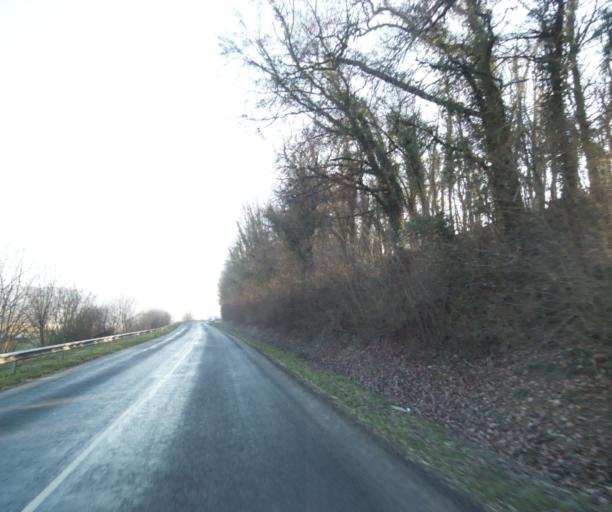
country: FR
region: Champagne-Ardenne
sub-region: Departement de la Haute-Marne
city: Chevillon
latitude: 48.5196
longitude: 5.1069
